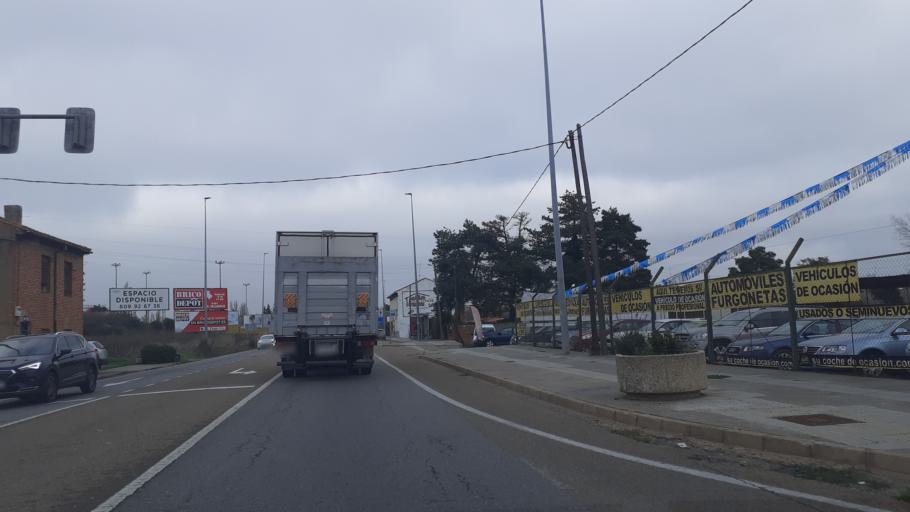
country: ES
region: Castille and Leon
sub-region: Provincia de Leon
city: Leon
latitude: 42.5664
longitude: -5.5823
